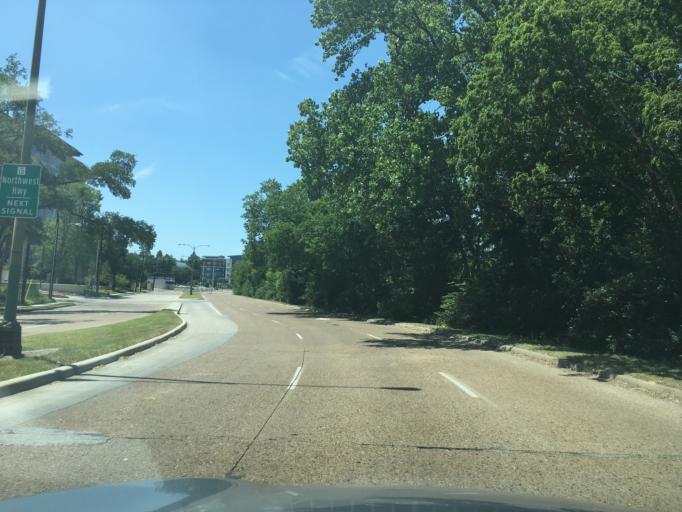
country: US
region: Texas
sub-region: Dallas County
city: Highland Park
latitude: 32.8535
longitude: -96.7292
